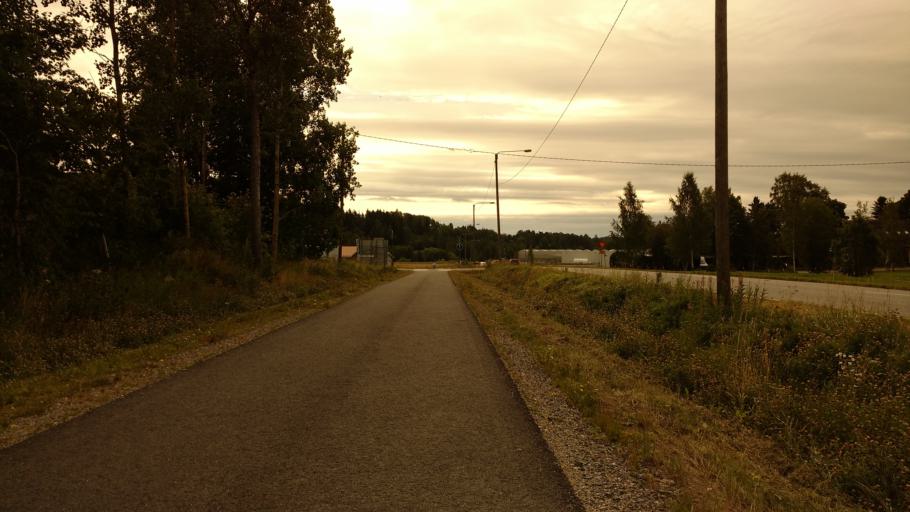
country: FI
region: Varsinais-Suomi
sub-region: Turku
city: Piikkioe
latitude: 60.4276
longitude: 22.4826
